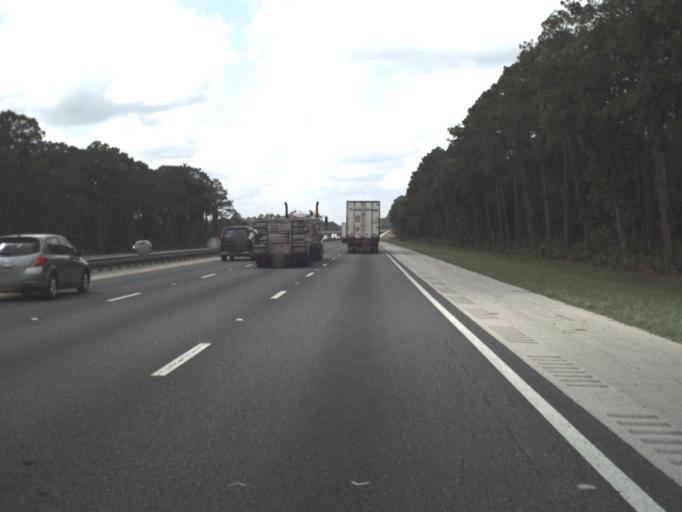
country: US
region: Florida
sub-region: Saint Johns County
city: Saint Augustine South
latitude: 29.8540
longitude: -81.3926
